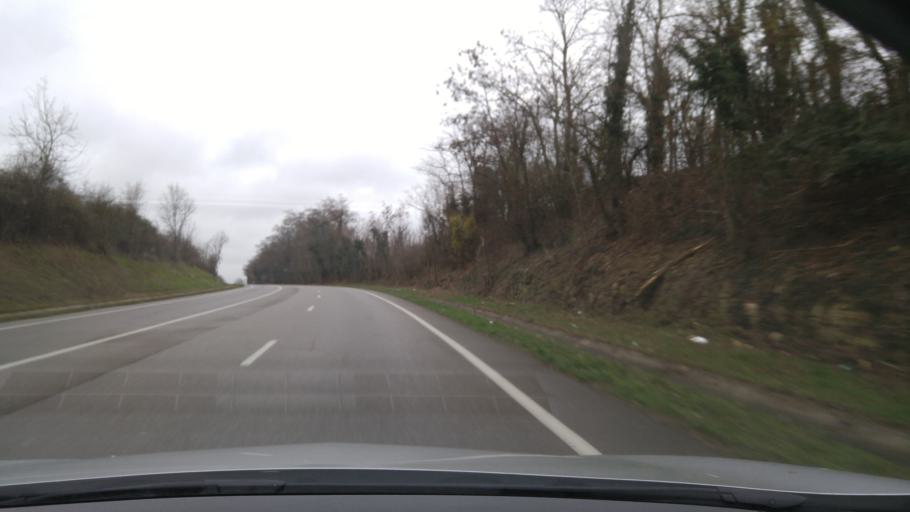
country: FR
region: Rhone-Alpes
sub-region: Departement de l'Isere
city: La Verpilliere
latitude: 45.6347
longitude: 5.1266
